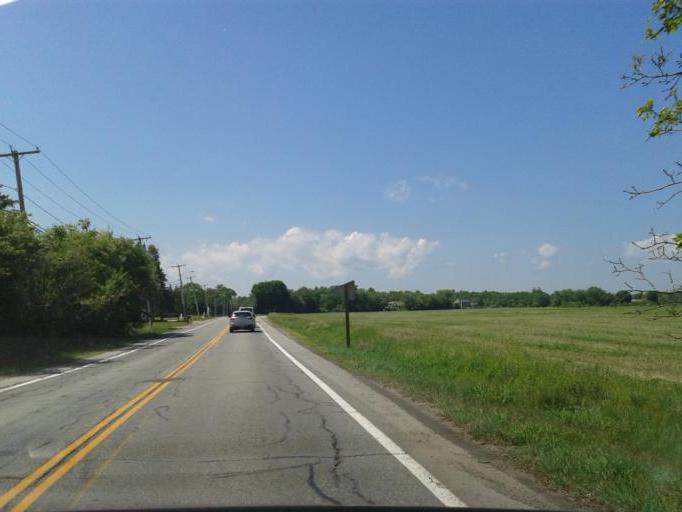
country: US
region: Rhode Island
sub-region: Washington County
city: Kingston
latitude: 41.4866
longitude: -71.5648
